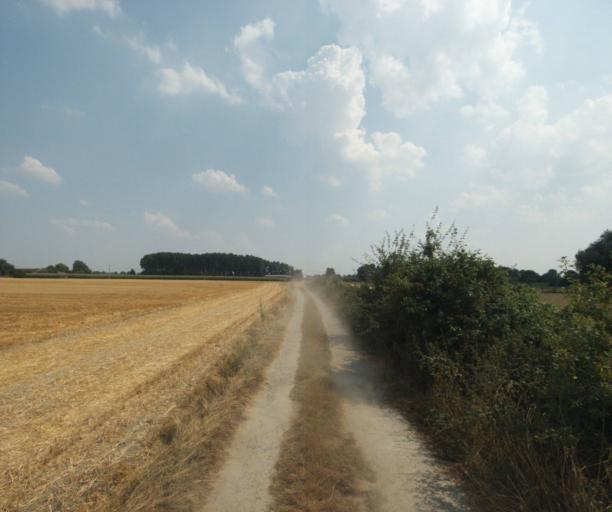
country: FR
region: Nord-Pas-de-Calais
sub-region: Departement du Nord
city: Quesnoy-sur-Deule
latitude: 50.7248
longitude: 3.0046
